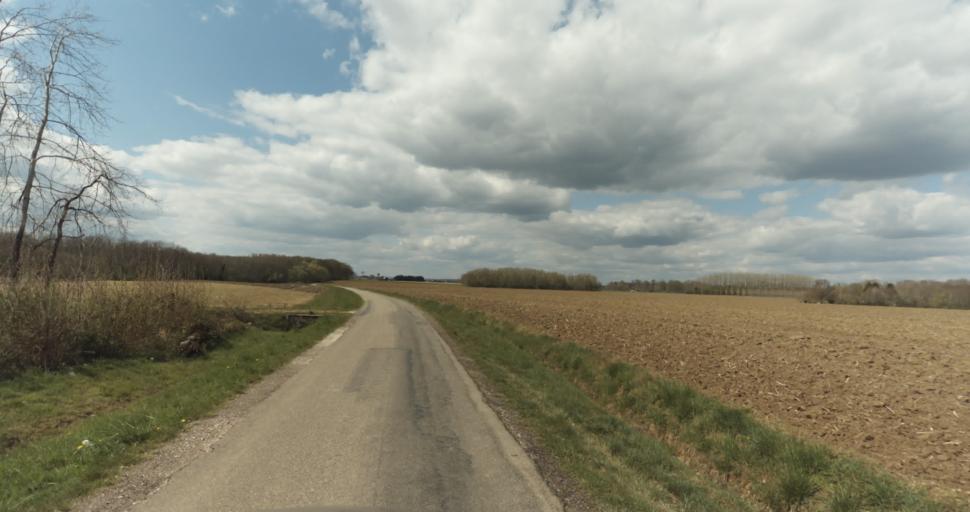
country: FR
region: Bourgogne
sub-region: Departement de la Cote-d'Or
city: Auxonne
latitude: 47.1717
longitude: 5.4215
